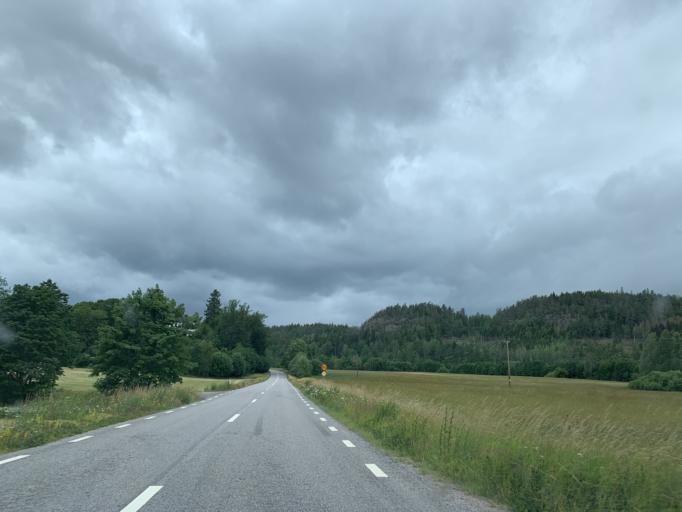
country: SE
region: Kalmar
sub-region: Vasterviks Kommun
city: Overum
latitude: 58.0151
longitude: 16.1677
